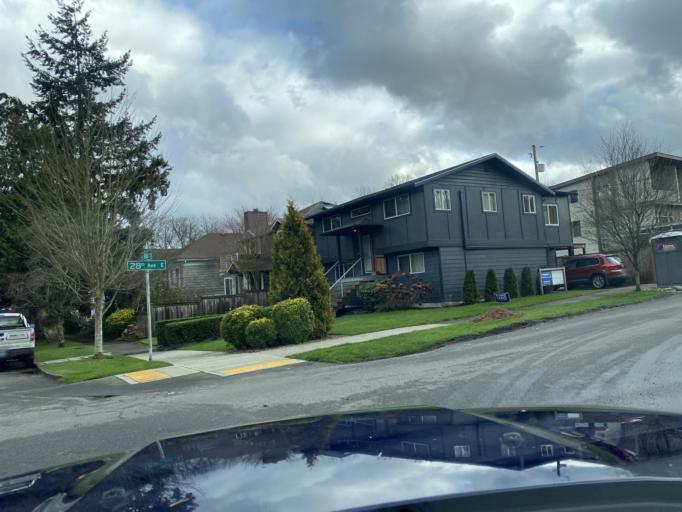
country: US
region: Washington
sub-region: King County
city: Seattle
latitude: 47.6267
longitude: -122.2965
